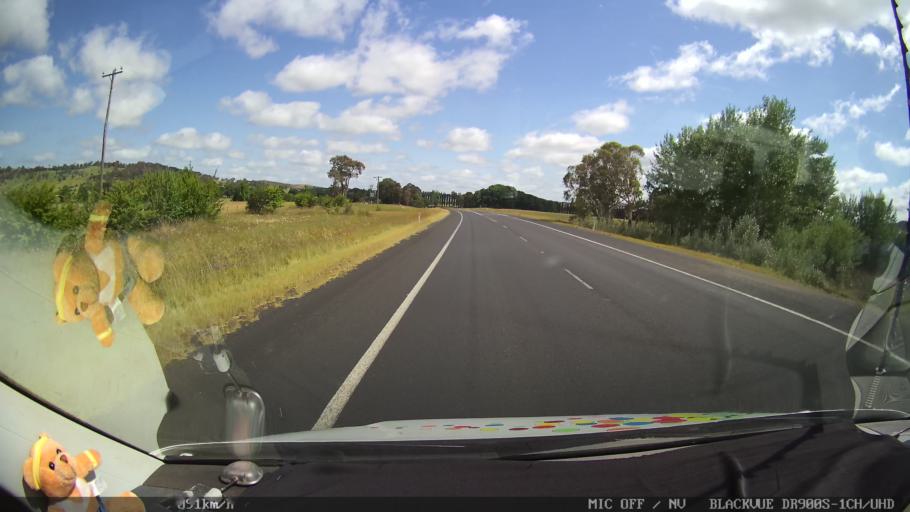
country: AU
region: New South Wales
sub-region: Glen Innes Severn
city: Glen Innes
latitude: -29.8644
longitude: 151.7376
